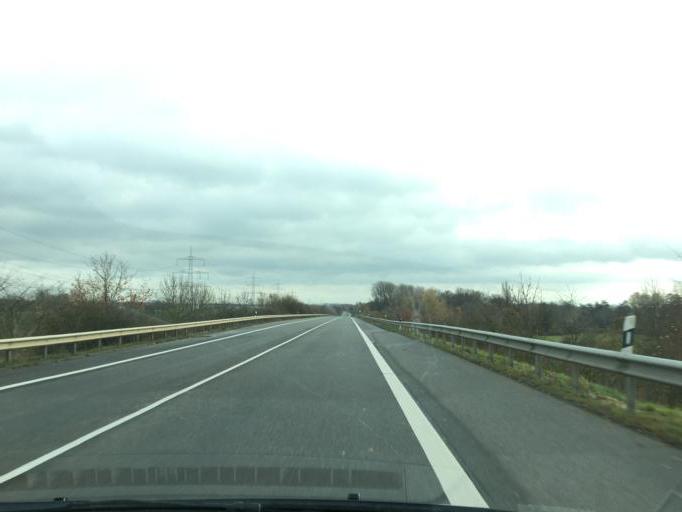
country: DE
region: North Rhine-Westphalia
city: Julich
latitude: 50.9021
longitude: 6.3669
